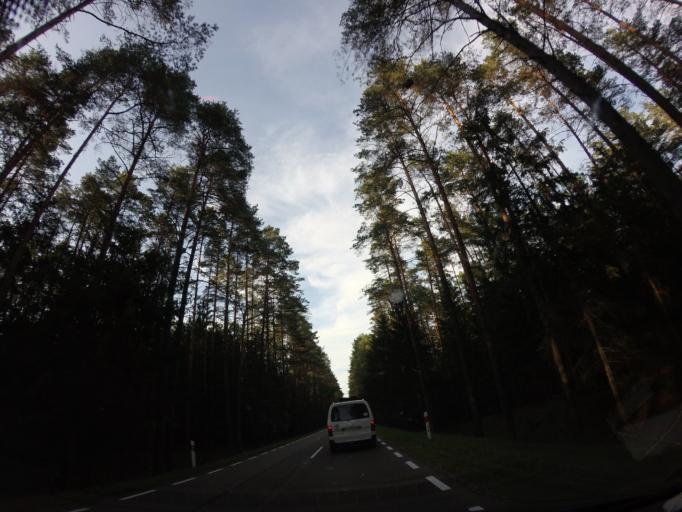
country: PL
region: Podlasie
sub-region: Powiat augustowski
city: Augustow
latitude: 53.8848
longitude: 23.1119
